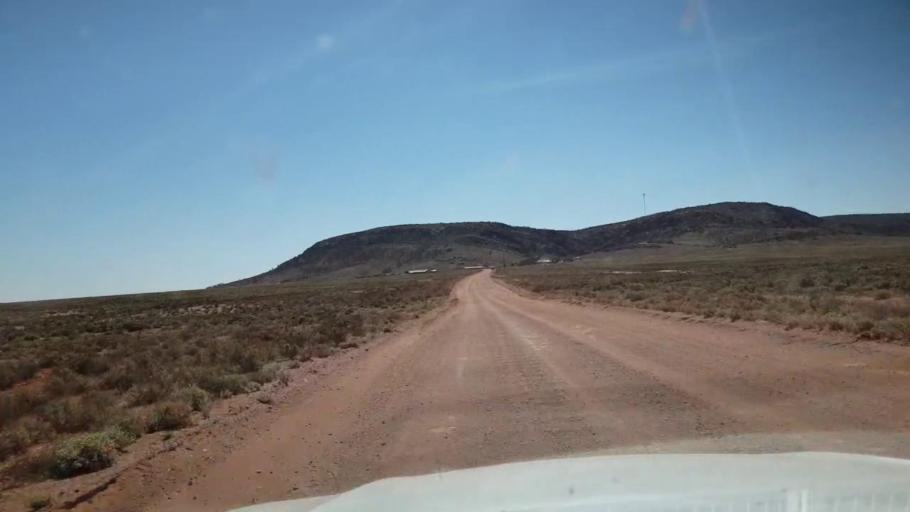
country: AU
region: South Australia
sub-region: Whyalla
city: Whyalla
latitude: -32.6934
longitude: 137.1300
